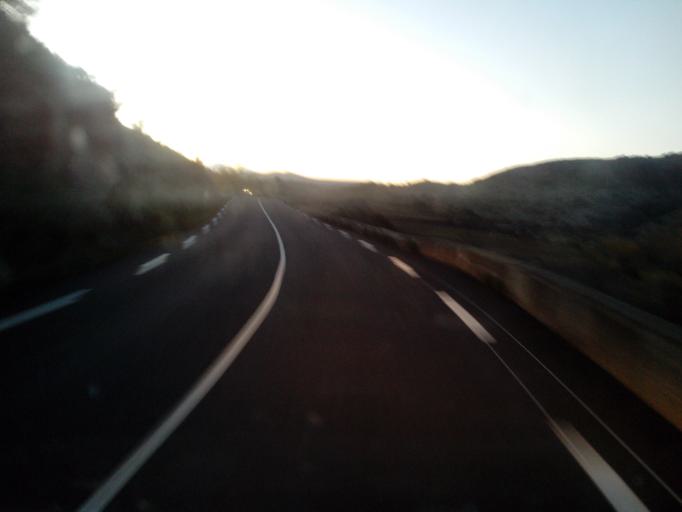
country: FR
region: Languedoc-Roussillon
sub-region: Departement des Pyrenees-Orientales
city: Estagel
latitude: 42.7767
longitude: 2.7303
